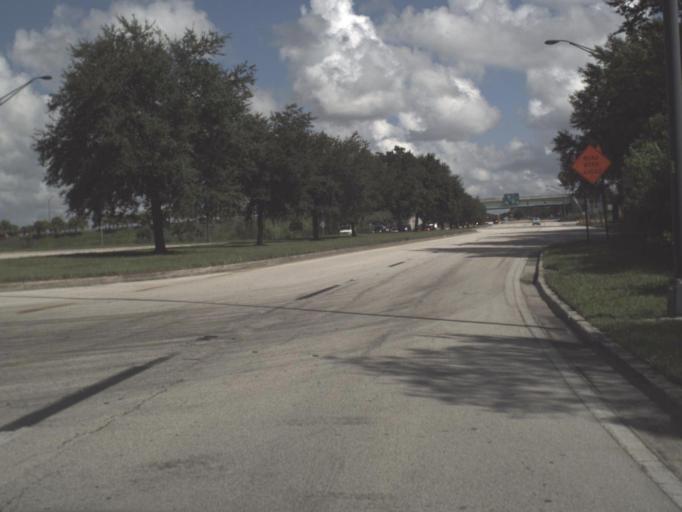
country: US
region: Florida
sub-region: Polk County
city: Medulla
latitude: 27.9932
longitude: -81.9761
